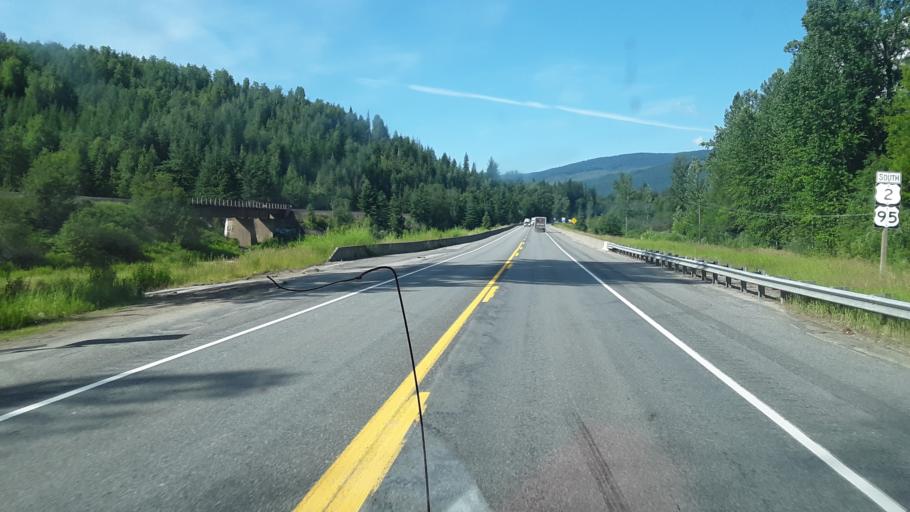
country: US
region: Idaho
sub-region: Bonner County
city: Ponderay
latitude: 48.4224
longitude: -116.4985
